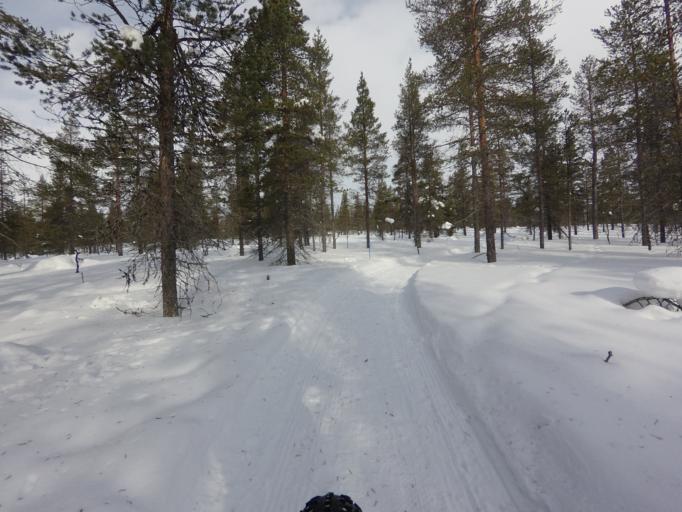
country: FI
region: Lapland
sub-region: Pohjois-Lappi
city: Ivalo
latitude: 68.3459
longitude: 27.4472
